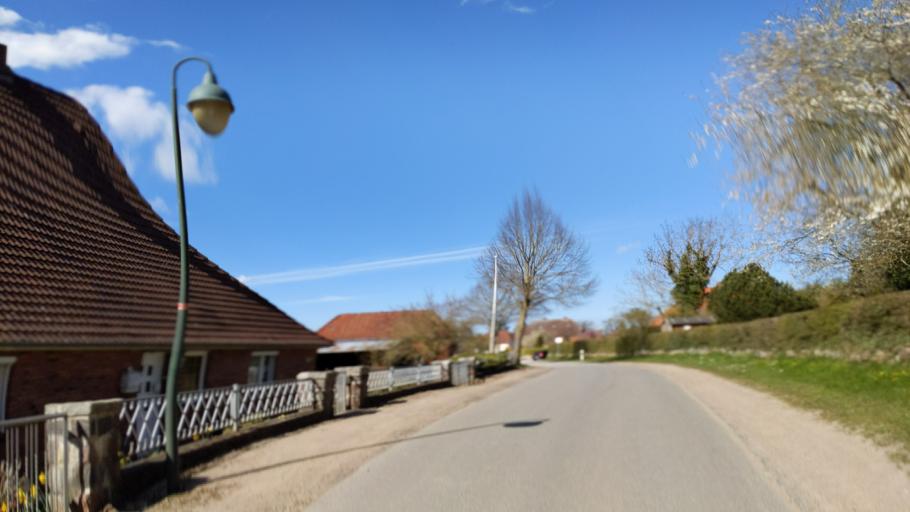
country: DE
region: Schleswig-Holstein
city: Kasseedorf
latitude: 54.1360
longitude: 10.6865
